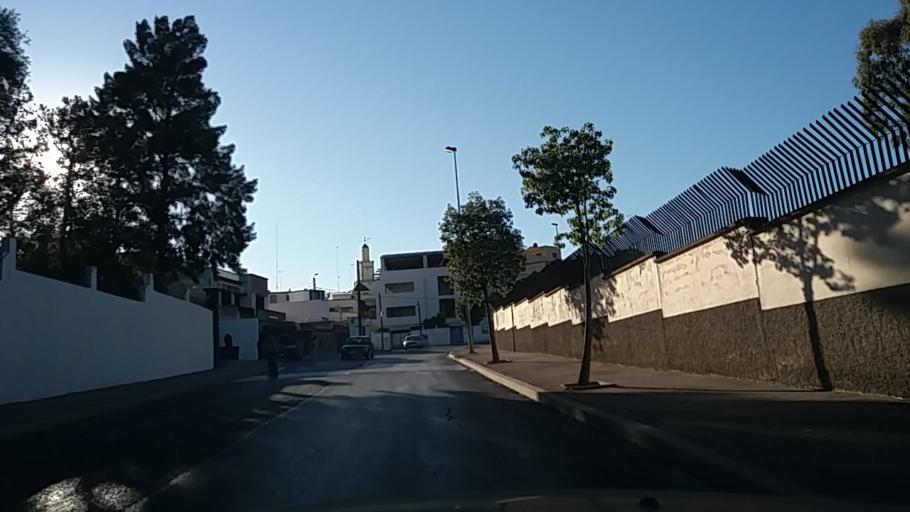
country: MA
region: Tanger-Tetouan
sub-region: Tanger-Assilah
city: Tangier
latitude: 35.7765
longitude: -5.8236
